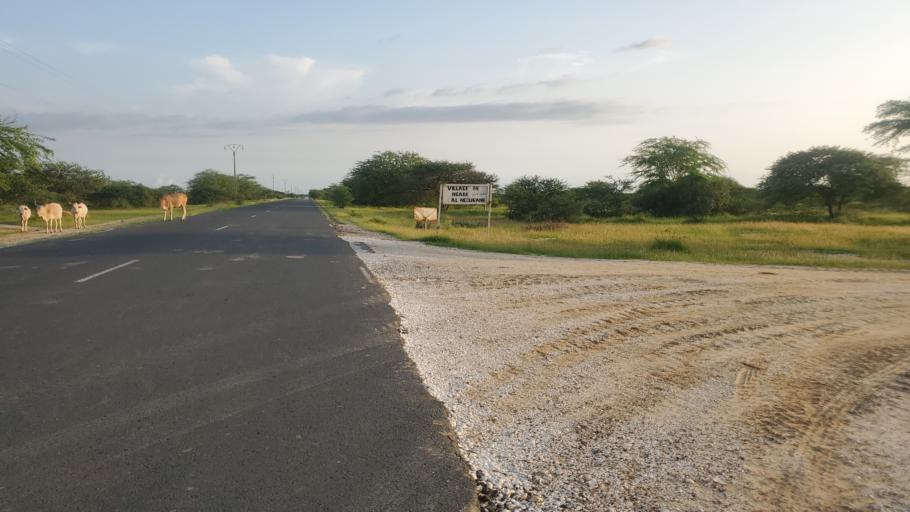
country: SN
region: Saint-Louis
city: Saint-Louis
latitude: 16.1867
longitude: -16.4094
